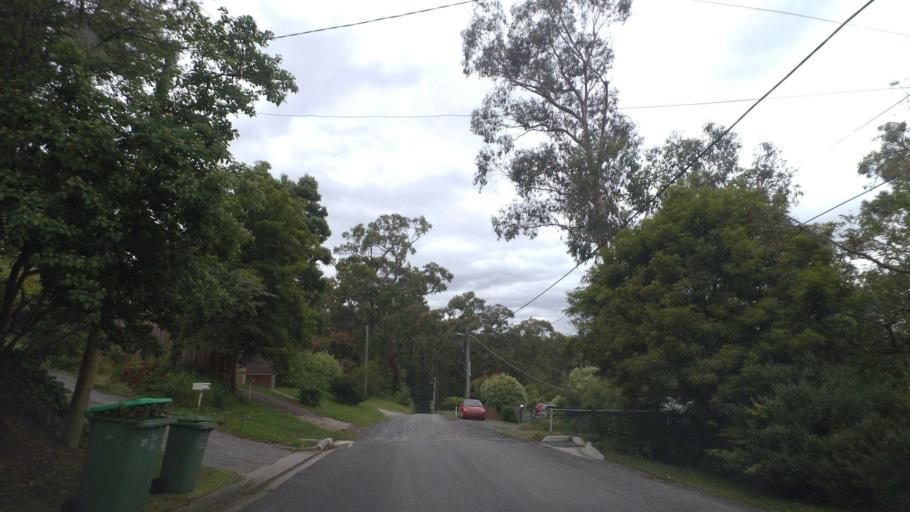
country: AU
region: Victoria
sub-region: Yarra Ranges
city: Mount Evelyn
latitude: -37.7907
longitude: 145.3813
